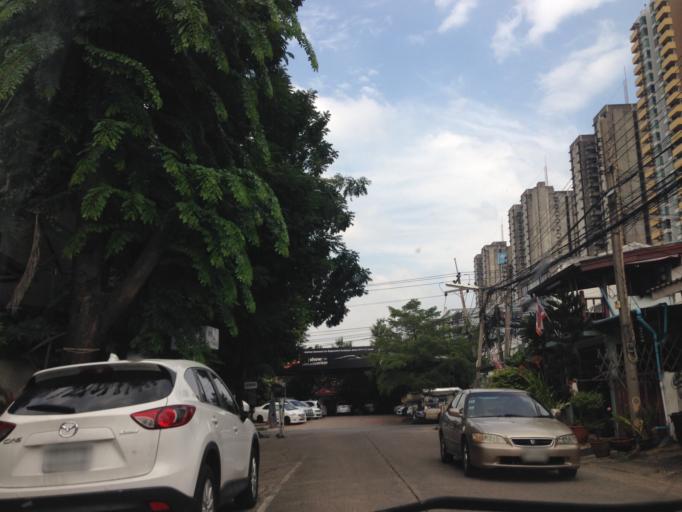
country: TH
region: Nonthaburi
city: Pak Kret
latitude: 13.9146
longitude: 100.5394
